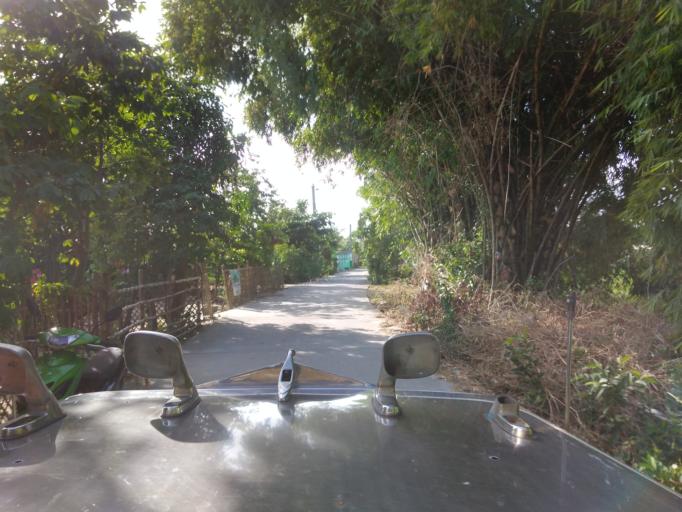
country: PH
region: Central Luzon
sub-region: Province of Pampanga
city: Malino
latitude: 15.1005
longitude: 120.6934
